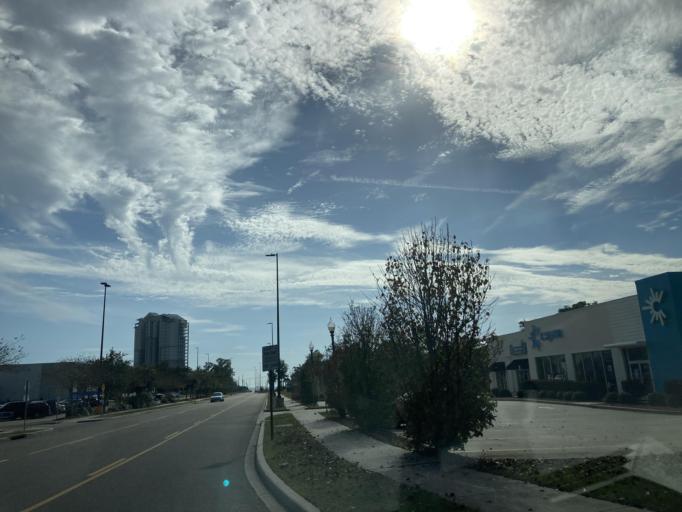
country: US
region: Mississippi
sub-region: Harrison County
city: West Gulfport
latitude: 30.3939
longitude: -88.9963
